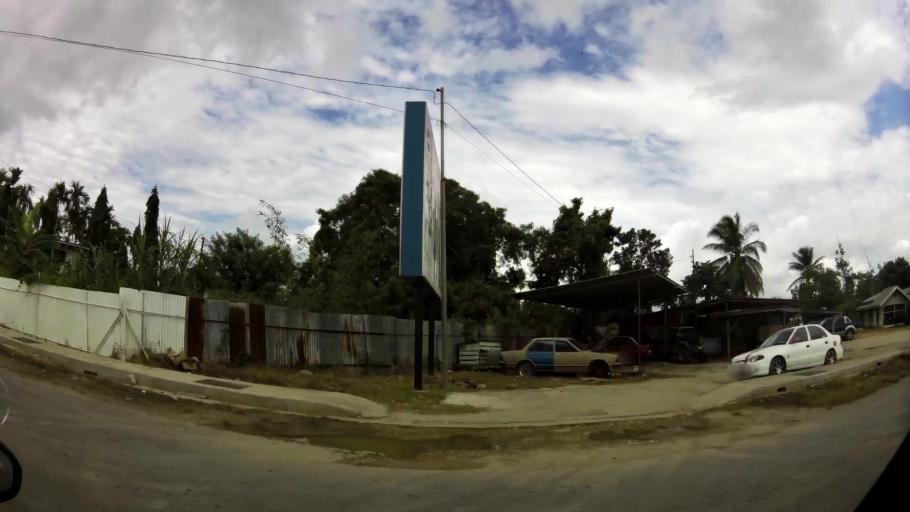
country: TT
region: Couva-Tabaquite-Talparo
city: Couva
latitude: 10.4592
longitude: -61.4283
